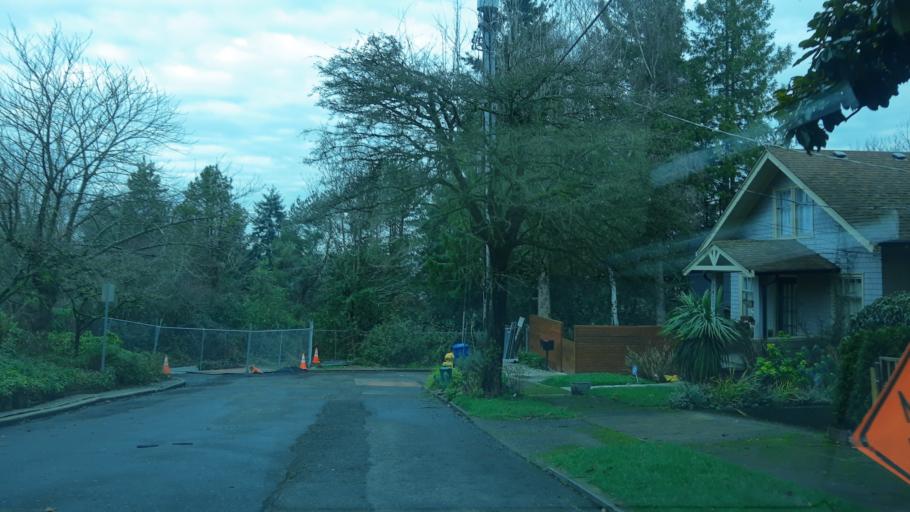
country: US
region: Washington
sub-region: King County
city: Seattle
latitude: 47.6418
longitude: -122.3190
